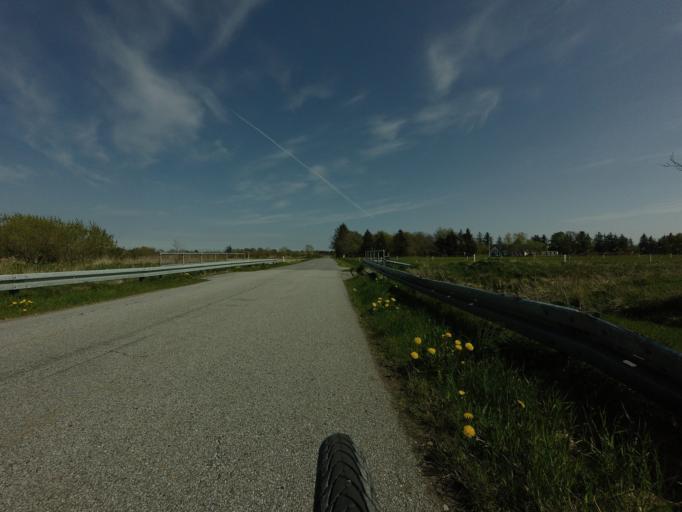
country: DK
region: North Denmark
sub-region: Jammerbugt Kommune
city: Pandrup
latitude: 57.2269
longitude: 9.6335
